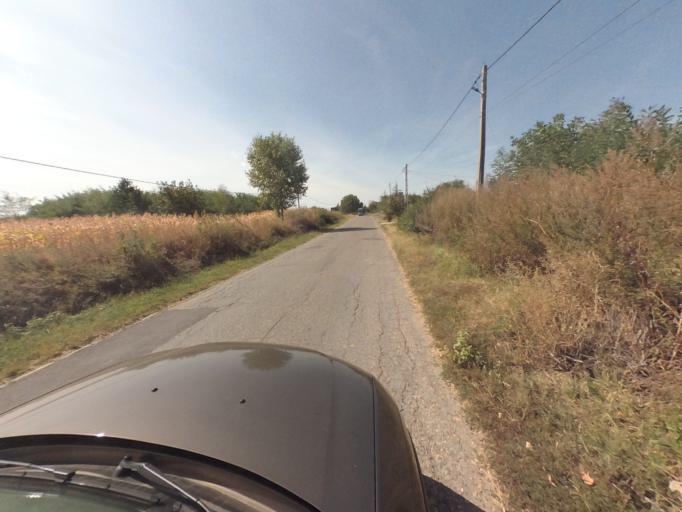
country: RO
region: Vaslui
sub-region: Comuna Deleni
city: Deleni
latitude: 46.5436
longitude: 27.7547
